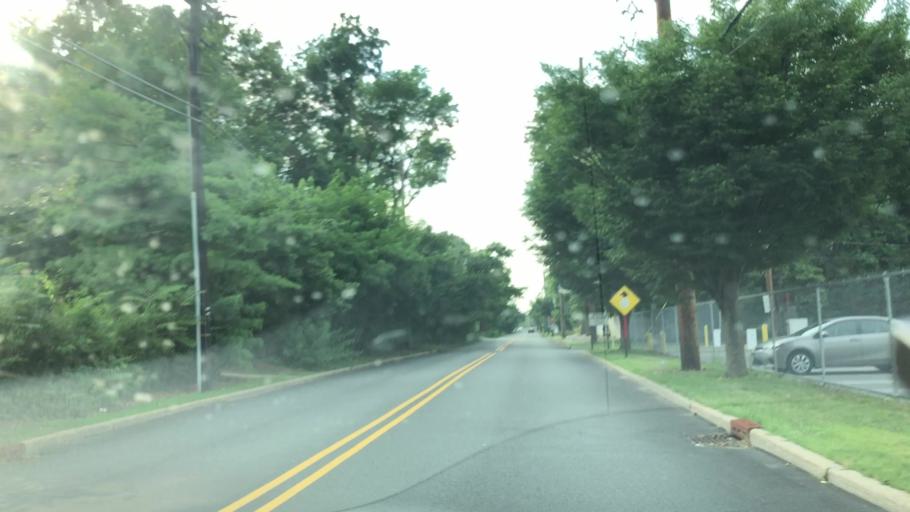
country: US
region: New Jersey
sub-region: Bergen County
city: Rochelle Park
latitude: 40.9157
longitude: -74.0801
